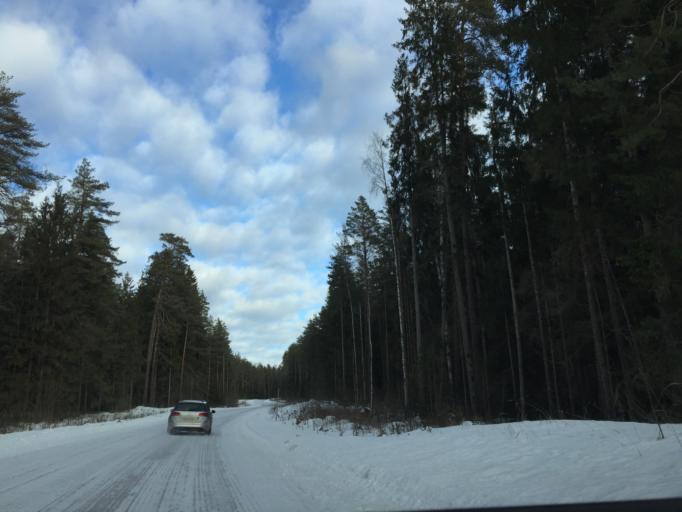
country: LV
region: Ogre
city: Jumprava
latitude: 56.5559
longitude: 24.9007
